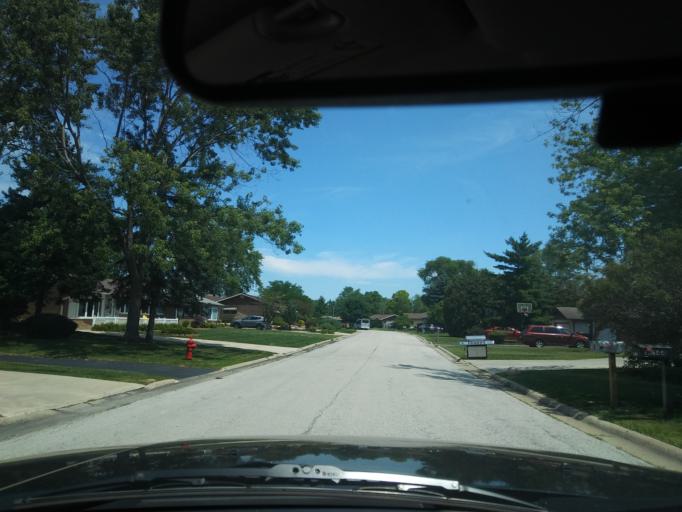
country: US
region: Illinois
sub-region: Cook County
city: Oak Forest
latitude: 41.5979
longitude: -87.7530
